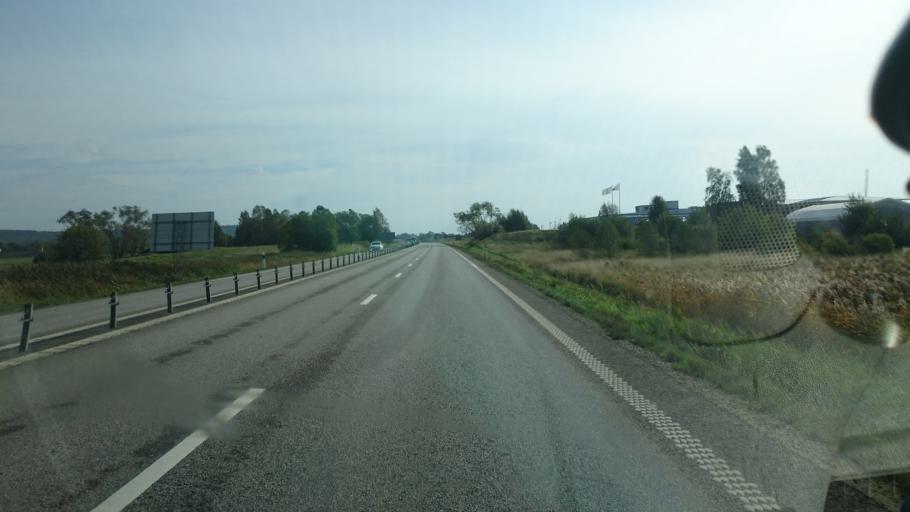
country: SE
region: Vaestra Goetaland
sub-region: Trollhattan
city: Trollhattan
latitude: 58.2976
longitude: 12.3496
